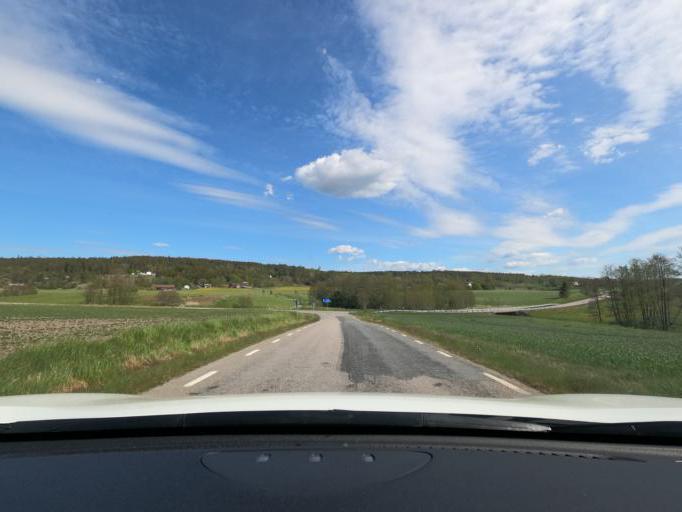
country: SE
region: Vaestra Goetaland
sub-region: Marks Kommun
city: Horred
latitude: 57.4540
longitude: 12.5061
